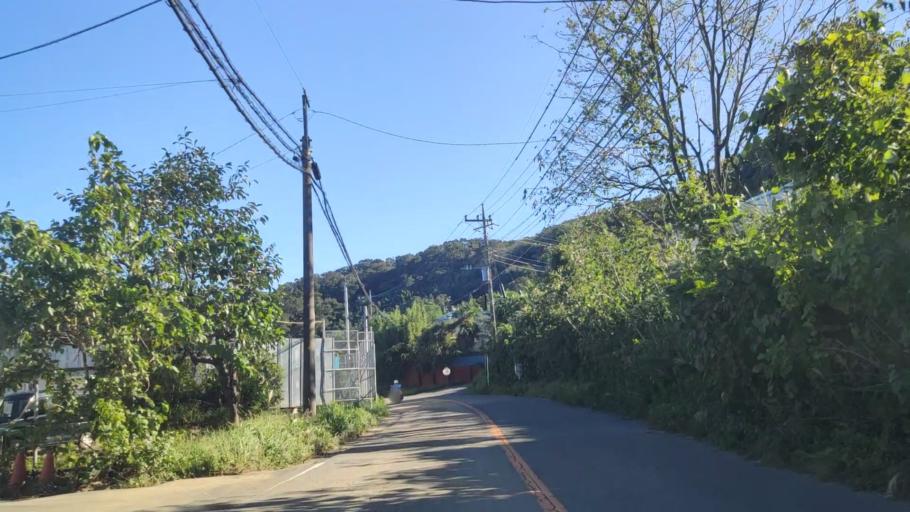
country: JP
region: Tokyo
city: Hachioji
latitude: 35.5663
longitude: 139.3130
